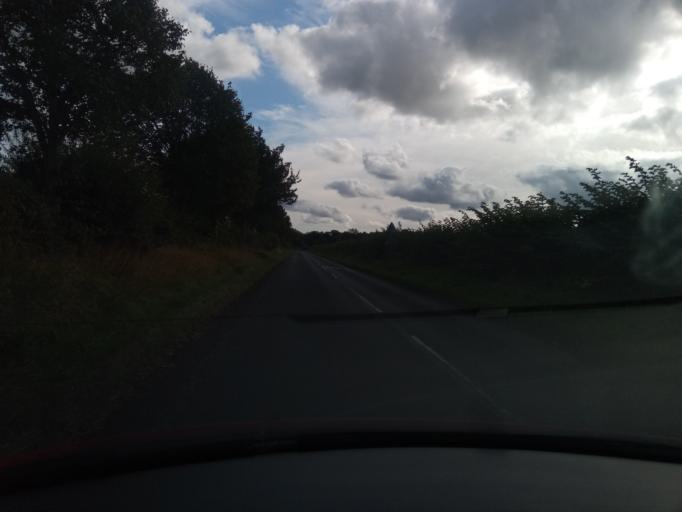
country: GB
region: Scotland
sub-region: The Scottish Borders
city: Kelso
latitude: 55.5267
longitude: -2.3583
